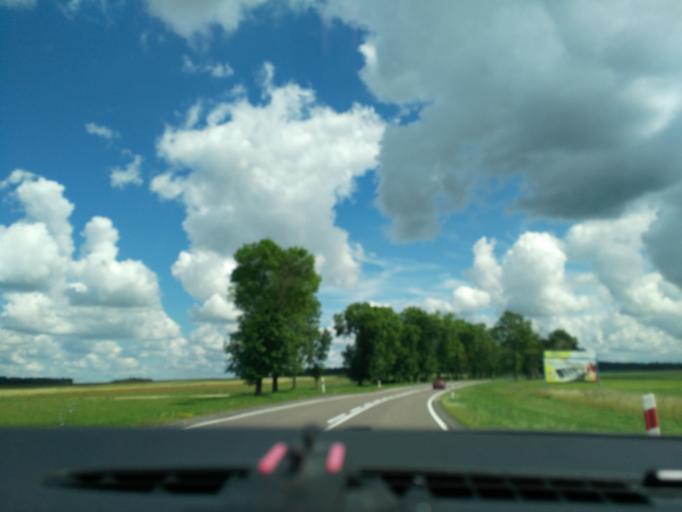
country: PL
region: Podlasie
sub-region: Powiat bielski
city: Bielsk Podlaski
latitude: 52.6982
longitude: 23.1251
